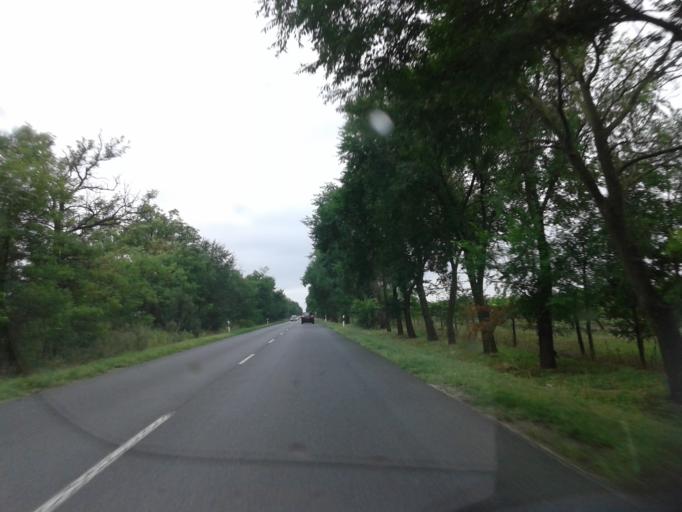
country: HU
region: Bacs-Kiskun
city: Solt
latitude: 46.8373
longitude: 19.0064
